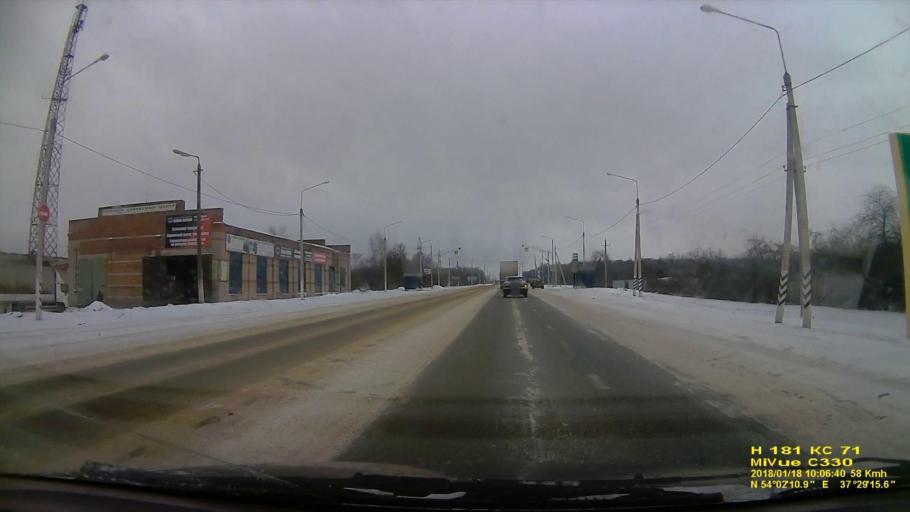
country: RU
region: Tula
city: Pervomayskiy
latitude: 54.0362
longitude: 37.4874
